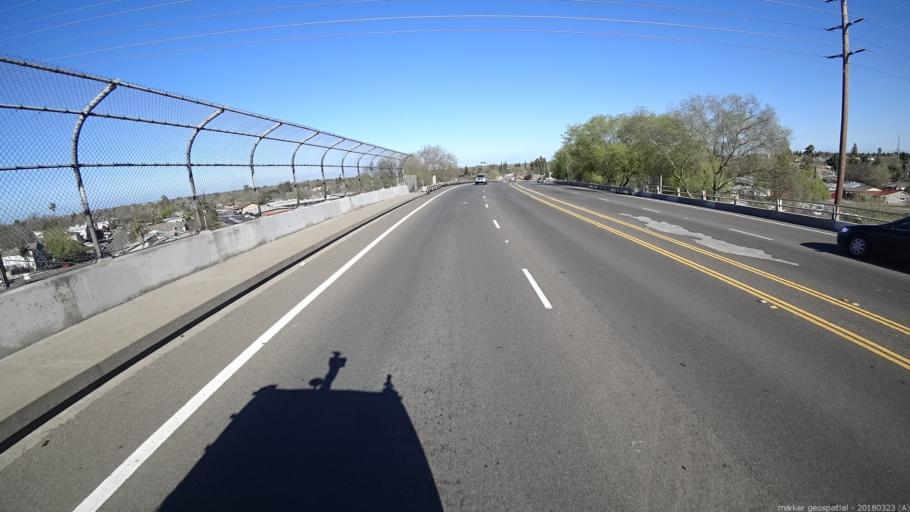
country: US
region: California
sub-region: Sacramento County
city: Foothill Farms
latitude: 38.6782
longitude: -121.3628
